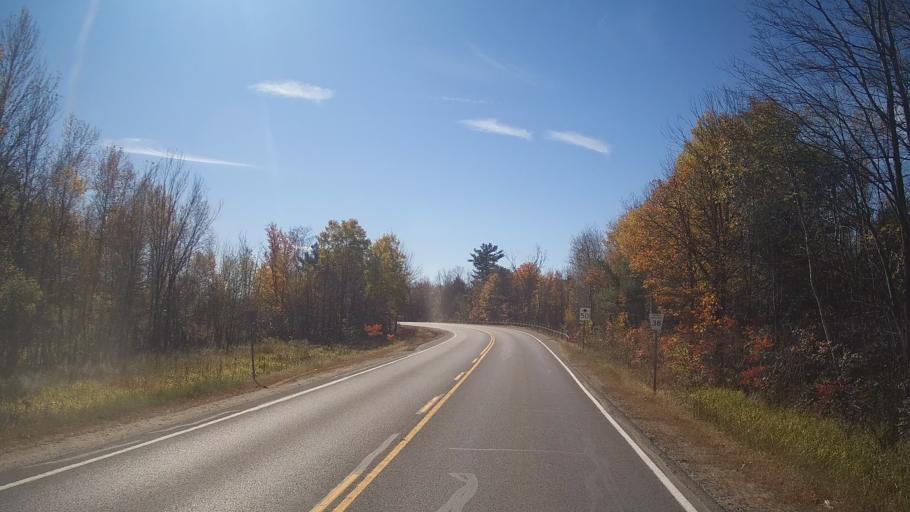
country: CA
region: Ontario
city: Kingston
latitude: 44.6692
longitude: -76.6762
